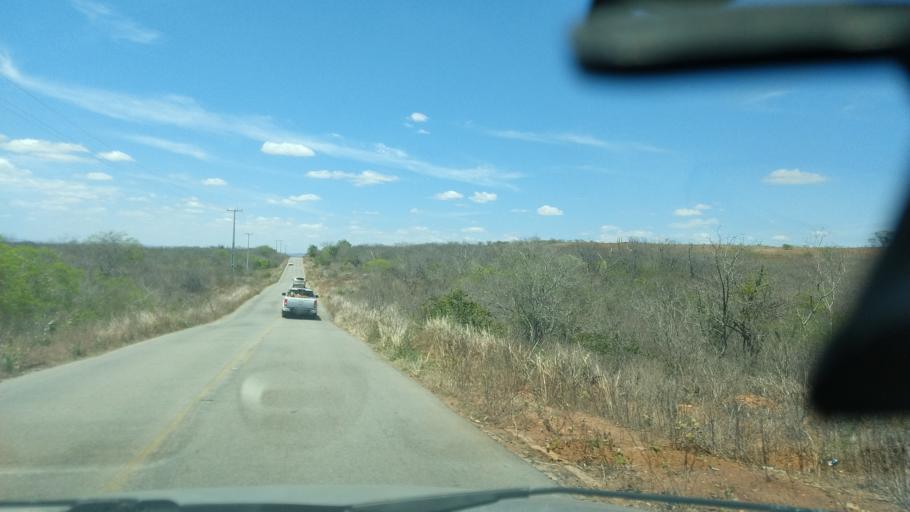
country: BR
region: Rio Grande do Norte
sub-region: Sao Paulo Do Potengi
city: Sao Paulo do Potengi
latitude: -5.9060
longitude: -35.6067
